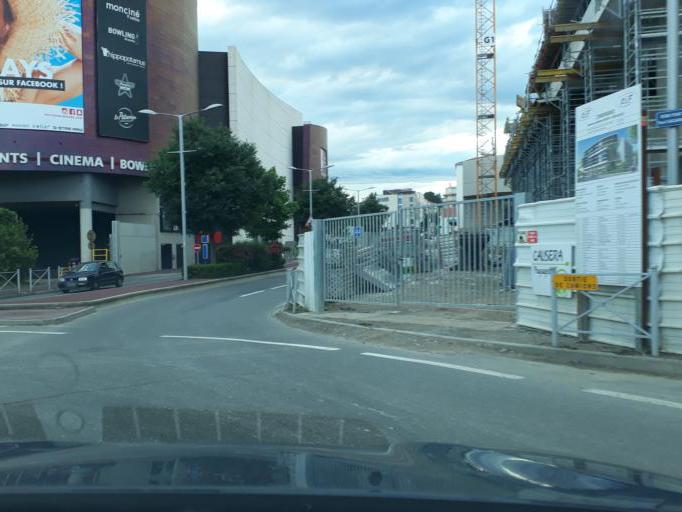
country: FR
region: Languedoc-Roussillon
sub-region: Departement de l'Herault
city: Beziers
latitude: 43.3351
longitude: 3.2282
